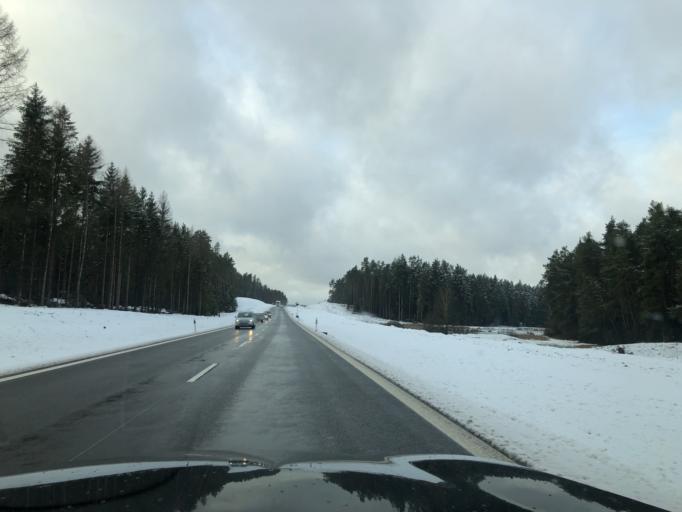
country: DE
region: Bavaria
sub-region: Upper Palatinate
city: Breitenbrunn
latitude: 49.3820
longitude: 12.0130
